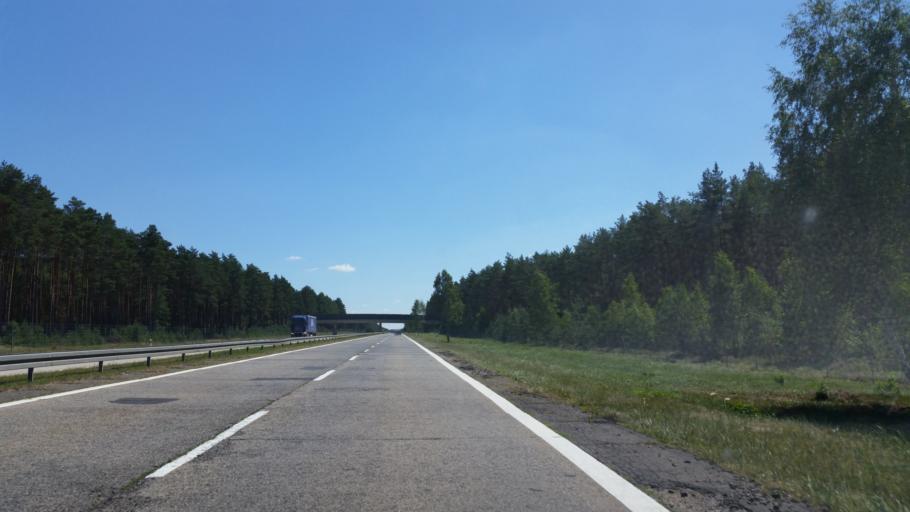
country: PL
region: Lubusz
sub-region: Powiat zaganski
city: Ilowa
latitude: 51.4509
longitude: 15.3344
